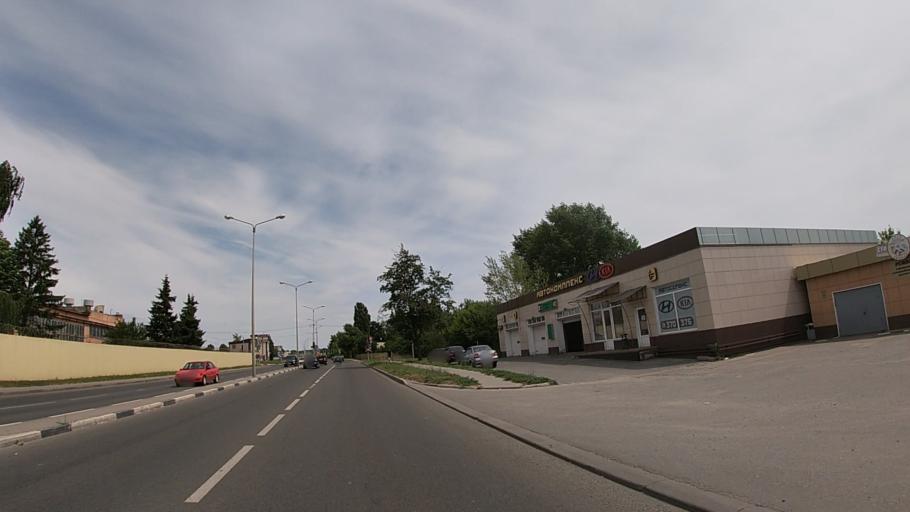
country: RU
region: Belgorod
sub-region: Belgorodskiy Rayon
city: Belgorod
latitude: 50.6166
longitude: 36.5383
